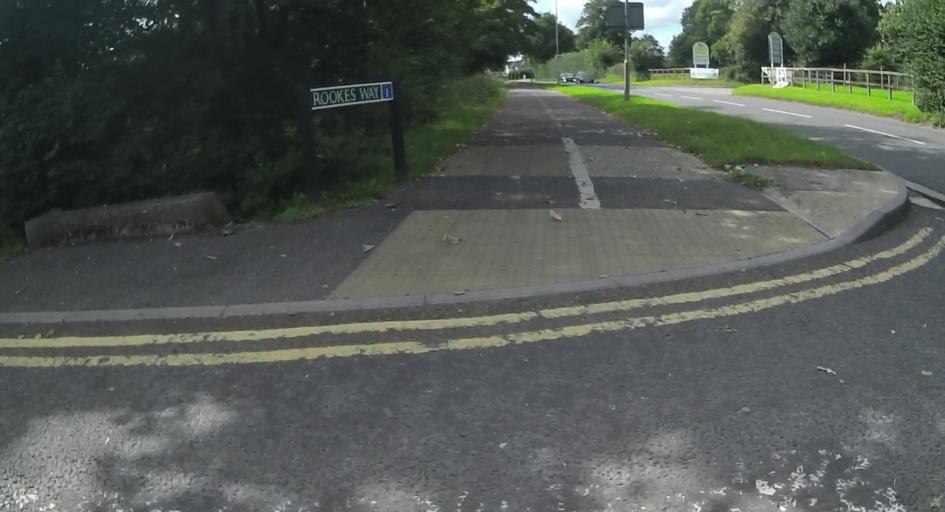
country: GB
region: England
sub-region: West Berkshire
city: Greenham
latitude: 51.4074
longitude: -1.2904
